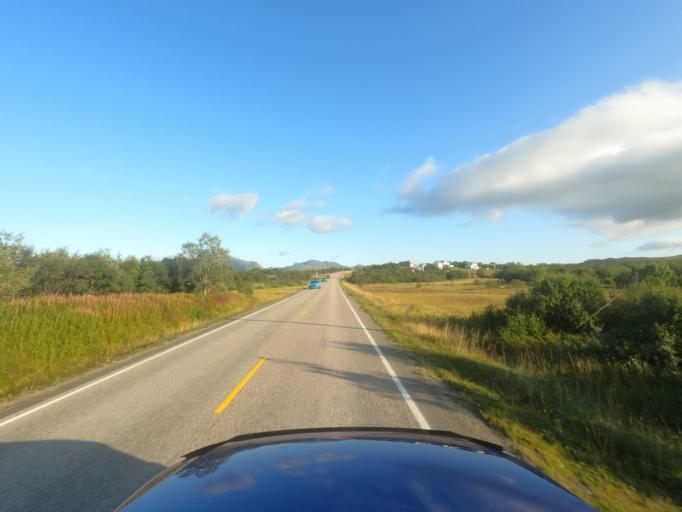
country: NO
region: Nordland
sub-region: Vestvagoy
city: Gravdal
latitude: 68.1519
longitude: 13.5397
